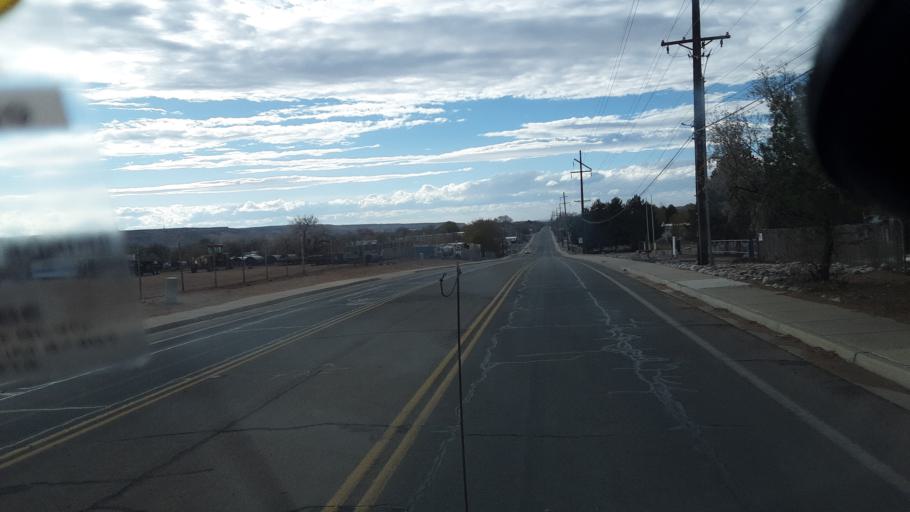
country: US
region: New Mexico
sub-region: San Juan County
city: Farmington
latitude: 36.7265
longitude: -108.1653
